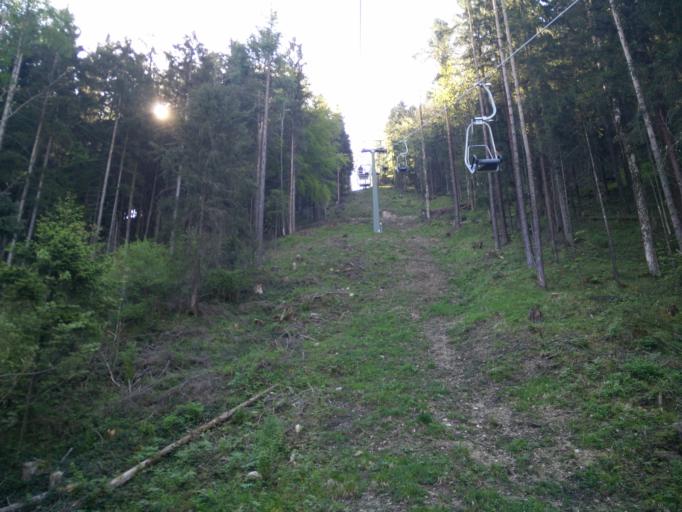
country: AT
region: Tyrol
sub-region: Politischer Bezirk Kufstein
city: Kufstein
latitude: 47.5893
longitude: 12.1880
